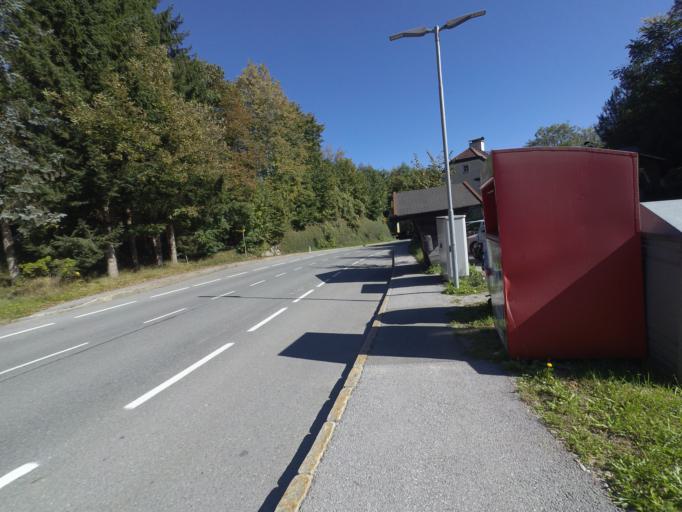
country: AT
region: Salzburg
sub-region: Politischer Bezirk Hallein
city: Hallein
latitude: 47.6809
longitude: 13.0890
